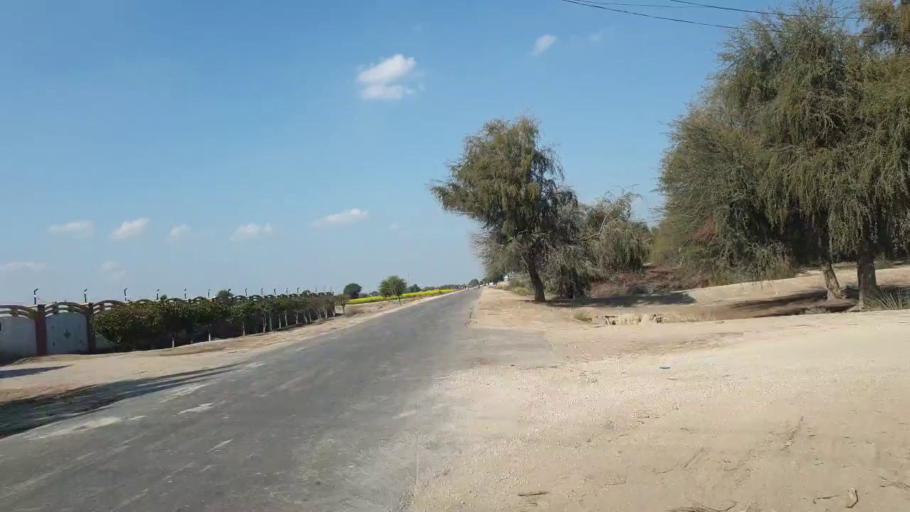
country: PK
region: Sindh
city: Shahpur Chakar
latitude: 26.0899
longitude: 68.5729
